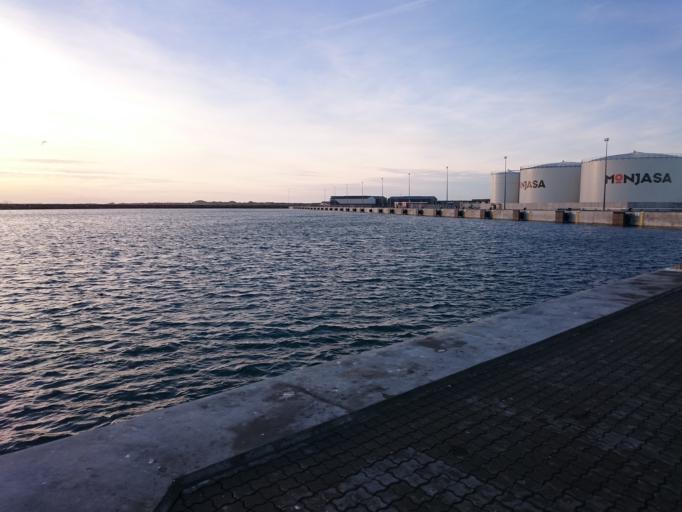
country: DK
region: North Denmark
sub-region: Frederikshavn Kommune
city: Skagen
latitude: 57.7137
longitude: 10.5921
